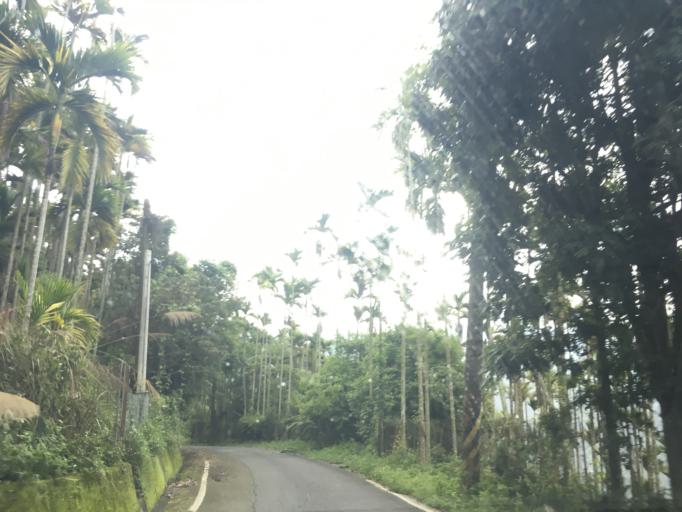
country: TW
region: Taiwan
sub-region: Yunlin
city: Douliu
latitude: 23.5691
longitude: 120.6337
